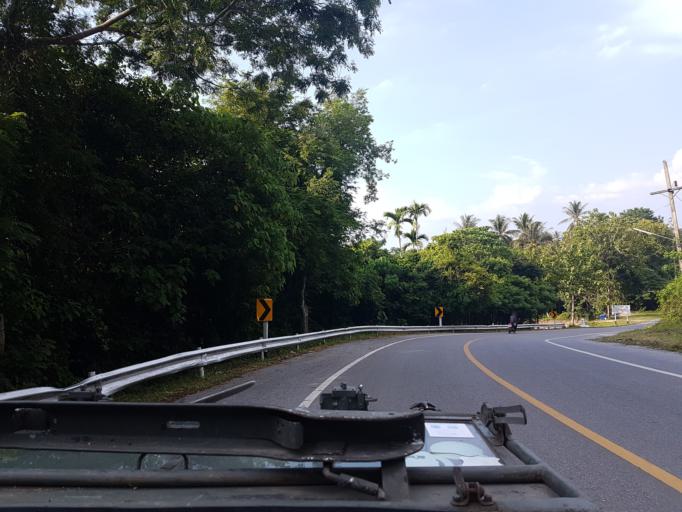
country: TH
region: Pattani
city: Khok Pho
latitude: 6.6595
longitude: 101.0946
